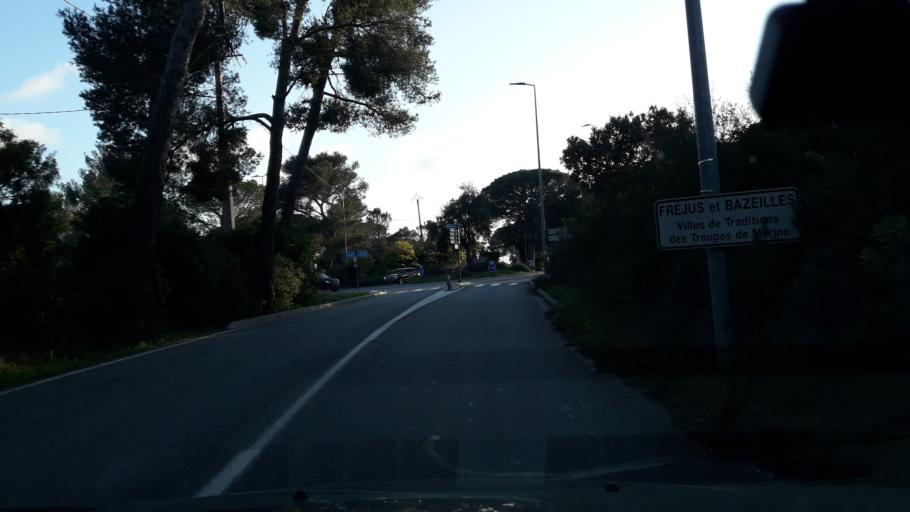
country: FR
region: Provence-Alpes-Cote d'Azur
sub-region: Departement du Var
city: Saint-Raphael
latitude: 43.4688
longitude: 6.7661
